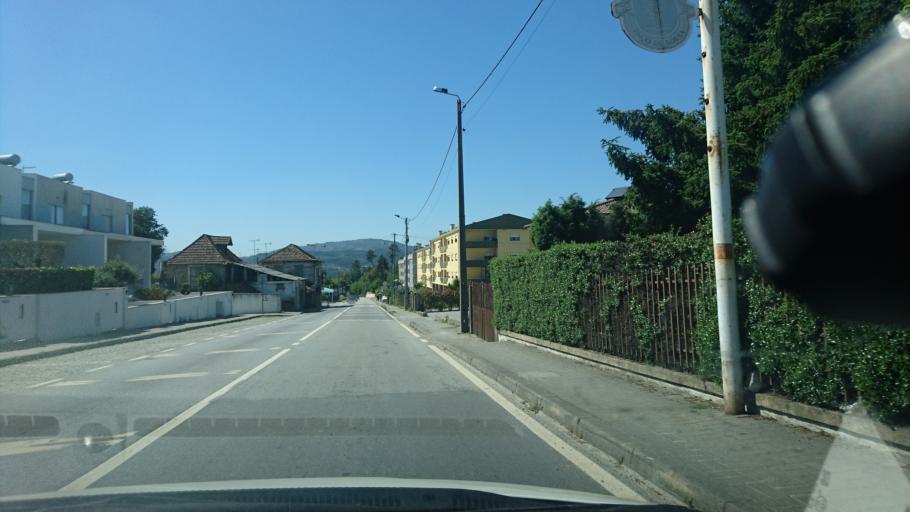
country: PT
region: Porto
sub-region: Paredes
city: Casteloes de Cepeda
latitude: 41.1705
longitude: -8.3309
